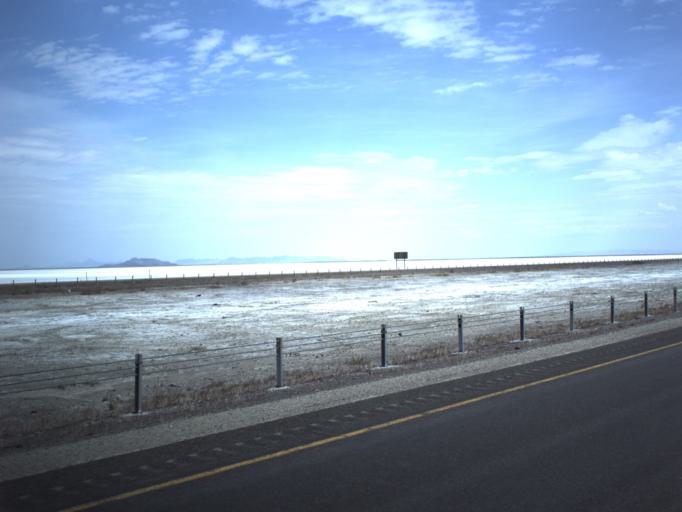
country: US
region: Utah
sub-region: Tooele County
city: Wendover
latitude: 40.7383
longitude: -113.8450
